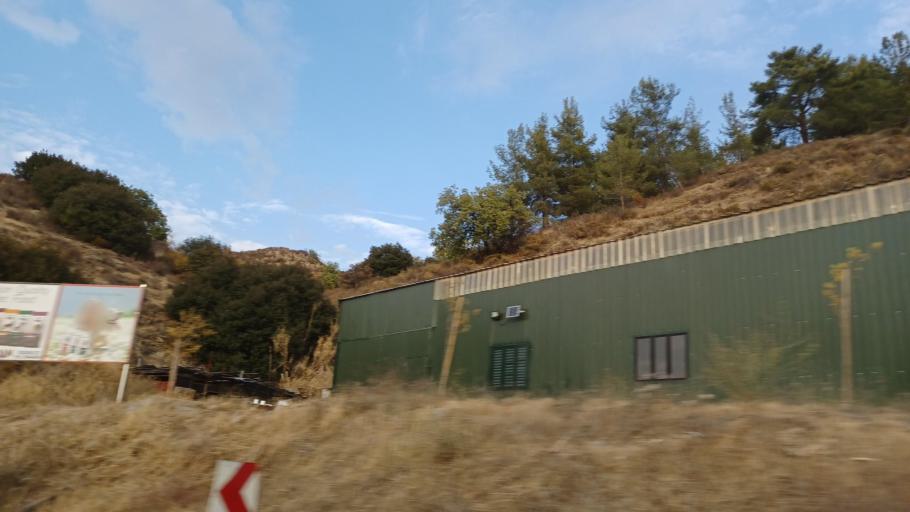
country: CY
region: Lefkosia
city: Kakopetria
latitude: 34.9883
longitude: 32.9067
